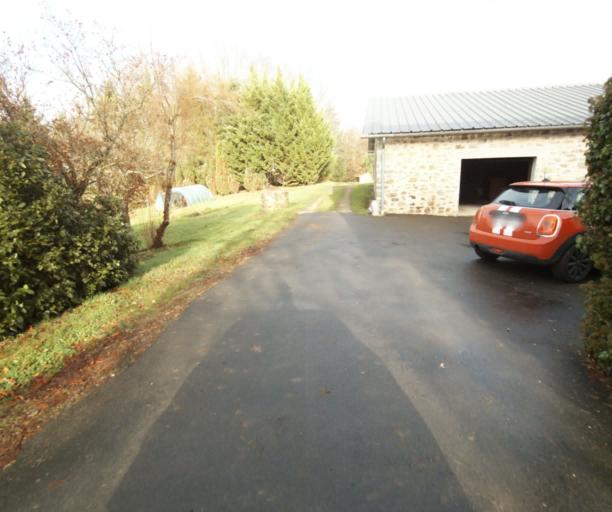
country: FR
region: Limousin
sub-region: Departement de la Correze
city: Saint-Mexant
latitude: 45.2806
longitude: 1.6096
